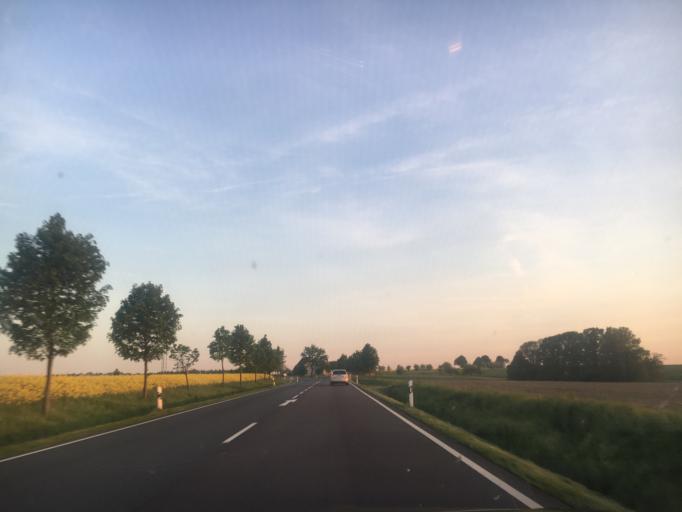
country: DE
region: Thuringia
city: Hirschfeld
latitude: 50.9851
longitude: 12.1373
